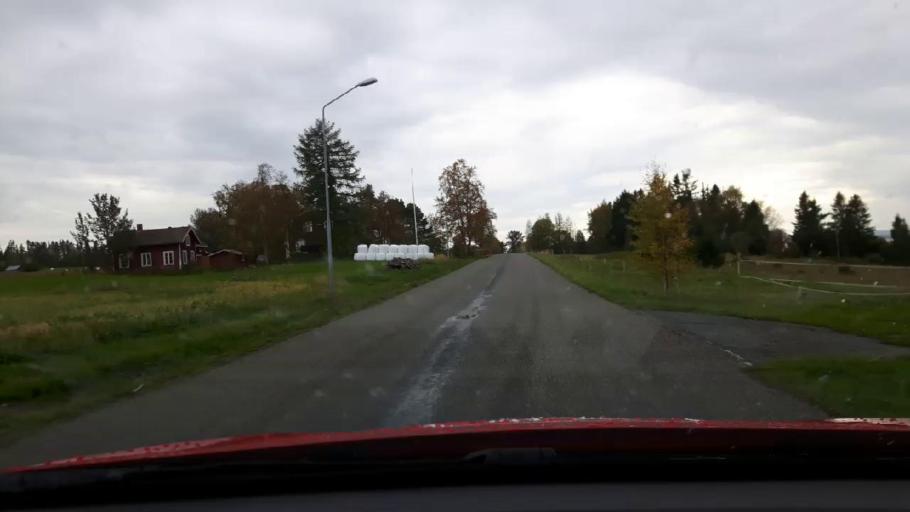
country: SE
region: Jaemtland
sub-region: Bergs Kommun
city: Hoverberg
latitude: 62.9608
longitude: 14.4899
